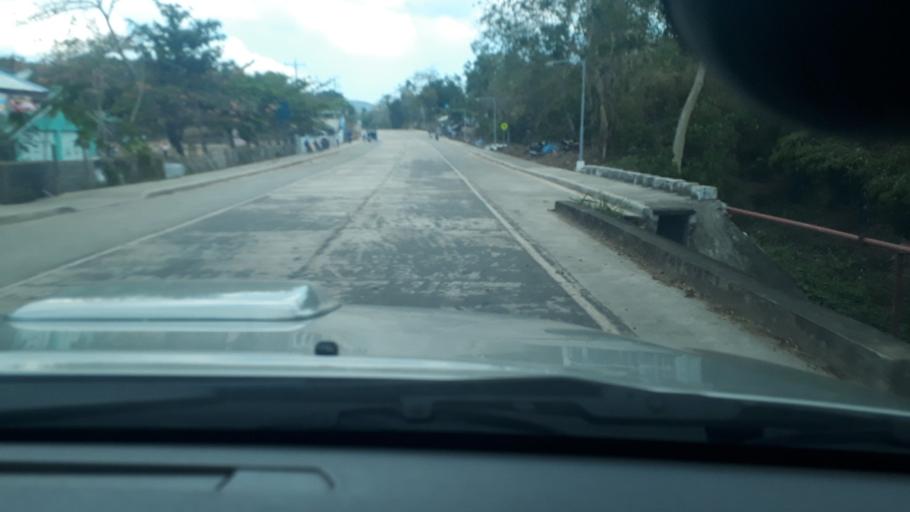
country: PH
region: Mimaropa
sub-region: Province of Palawan
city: Salvacion
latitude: 12.1354
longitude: 119.9371
